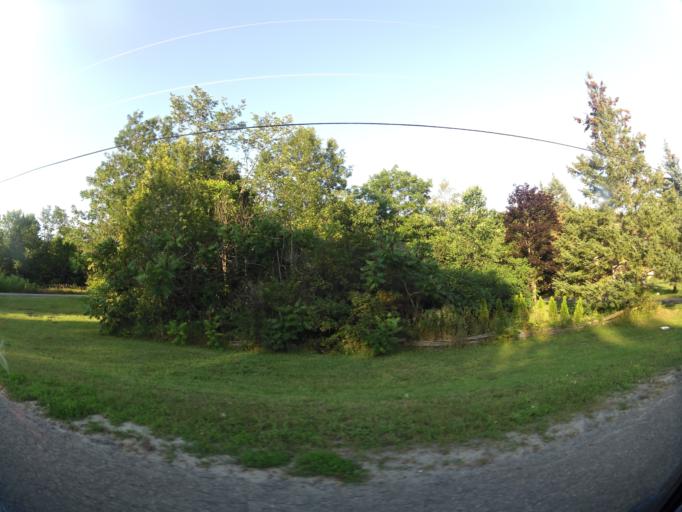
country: CA
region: Ontario
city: Clarence-Rockland
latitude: 45.5034
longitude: -75.4118
